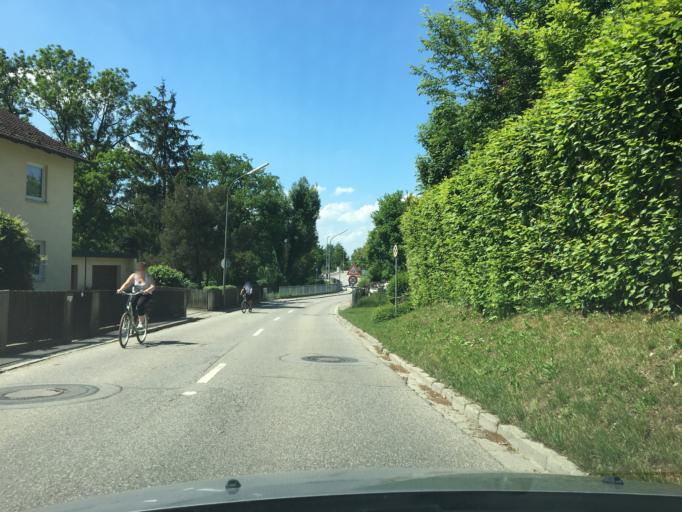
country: DE
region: Bavaria
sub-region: Upper Bavaria
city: Haimhausen
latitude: 48.3171
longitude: 11.5515
